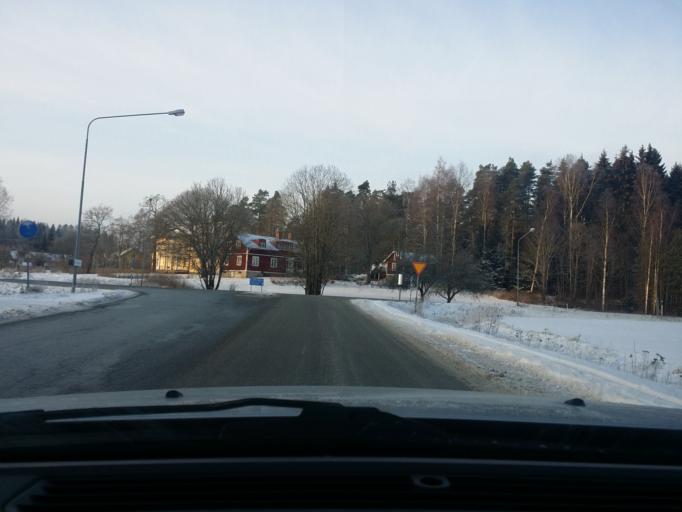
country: SE
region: OErebro
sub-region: Lindesbergs Kommun
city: Lindesberg
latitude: 59.6017
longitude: 15.1862
